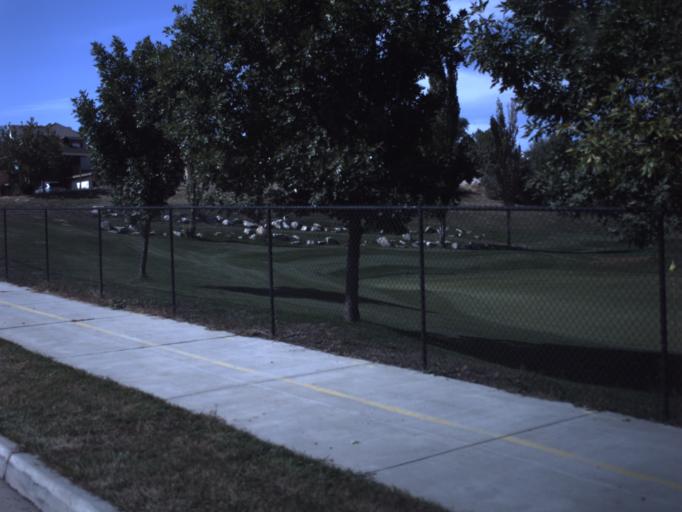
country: US
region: Utah
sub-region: Salt Lake County
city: South Jordan
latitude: 40.5591
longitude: -111.9130
